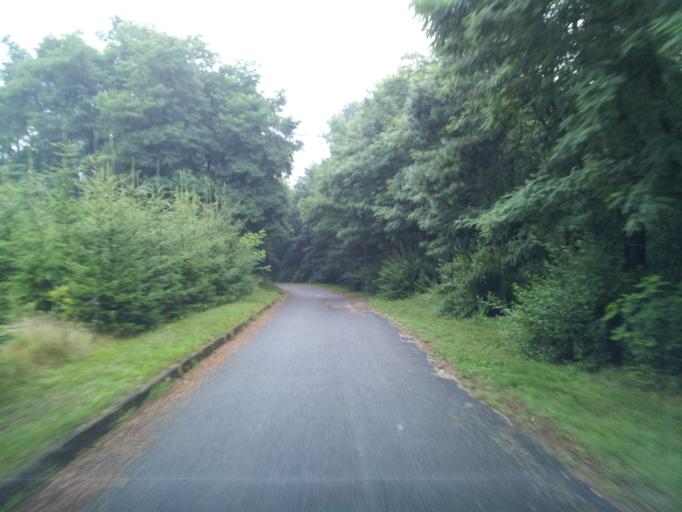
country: HU
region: Zala
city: Zalalovo
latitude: 46.8653
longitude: 16.5517
